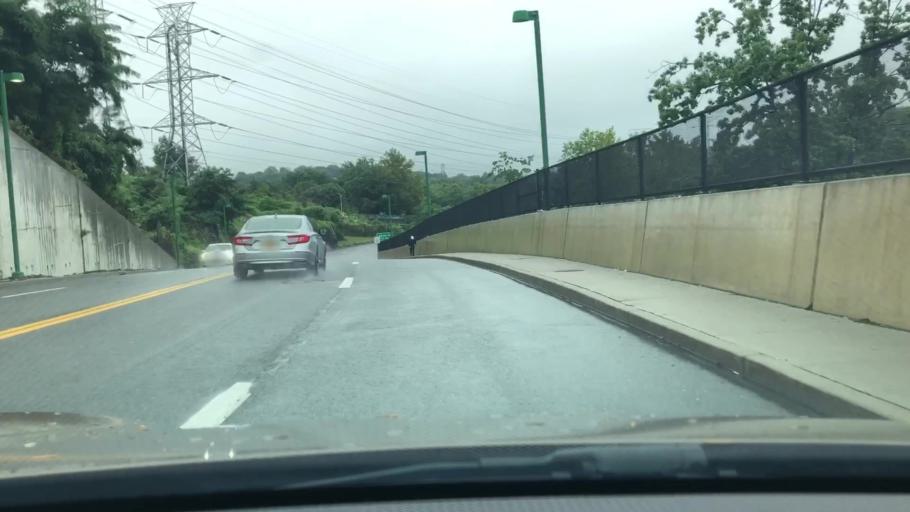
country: US
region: New York
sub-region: Westchester County
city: Tuckahoe
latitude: 40.9555
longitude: -73.8570
